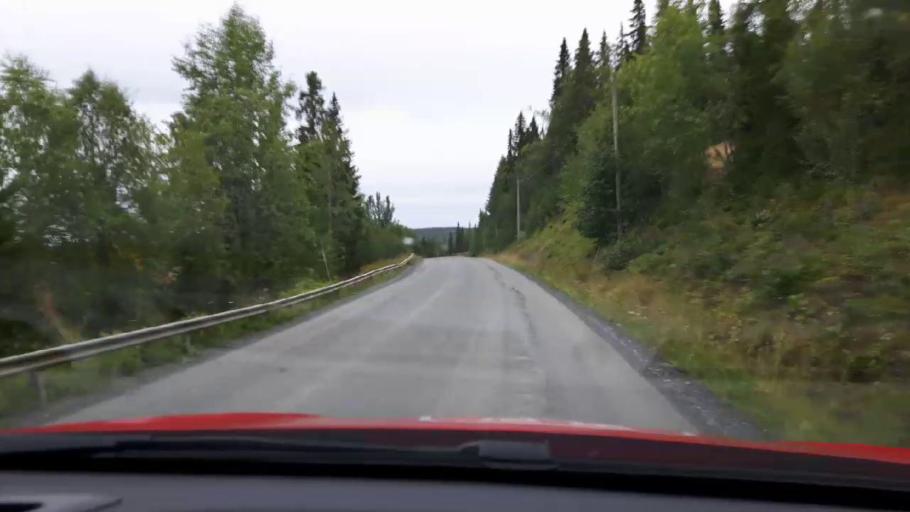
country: SE
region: Jaemtland
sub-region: Are Kommun
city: Jarpen
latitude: 63.4085
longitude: 13.3578
